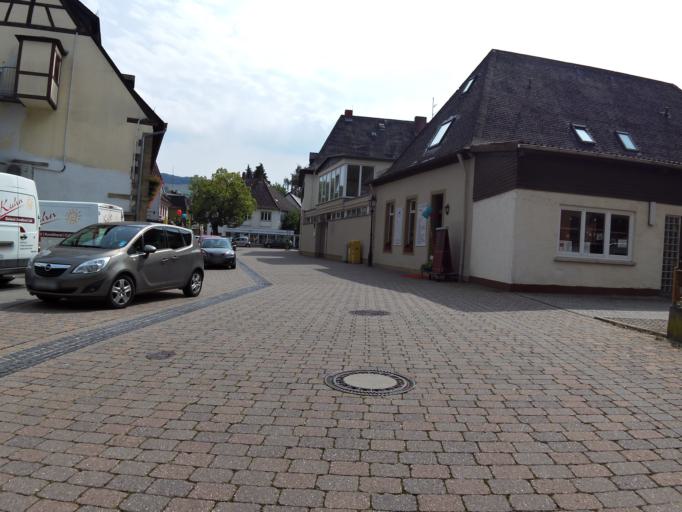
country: DE
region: Rheinland-Pfalz
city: Rockenhausen
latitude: 49.6291
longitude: 7.8187
